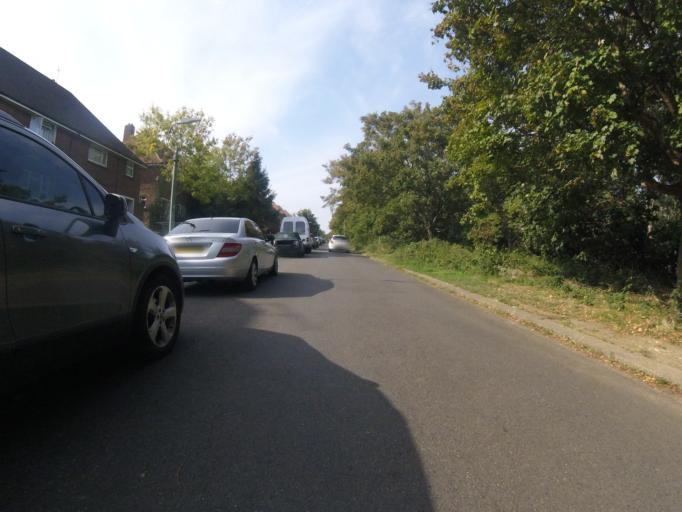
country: GB
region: England
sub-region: Brighton and Hove
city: Hove
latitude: 50.8507
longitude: -0.1858
